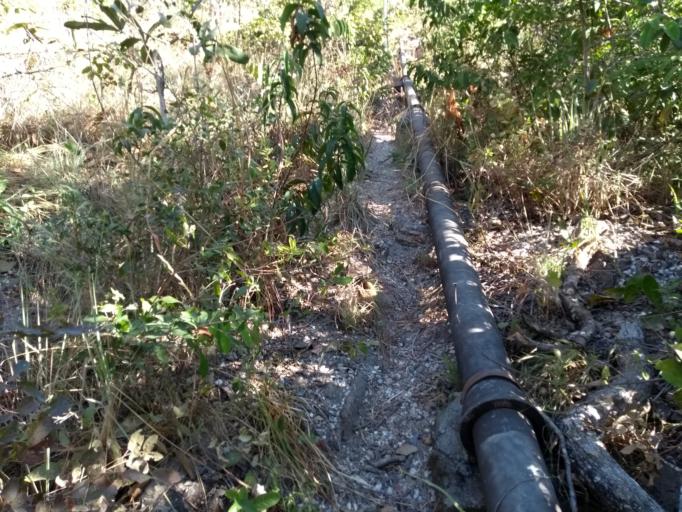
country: BR
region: Goias
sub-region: Cavalcante
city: Cavalcante
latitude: -13.8002
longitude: -47.4493
